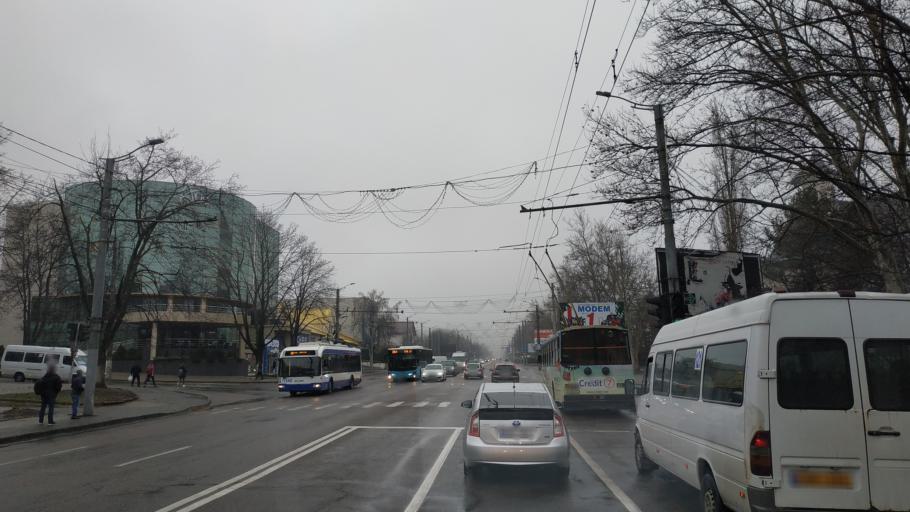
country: MD
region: Chisinau
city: Vatra
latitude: 47.0290
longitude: 28.7891
